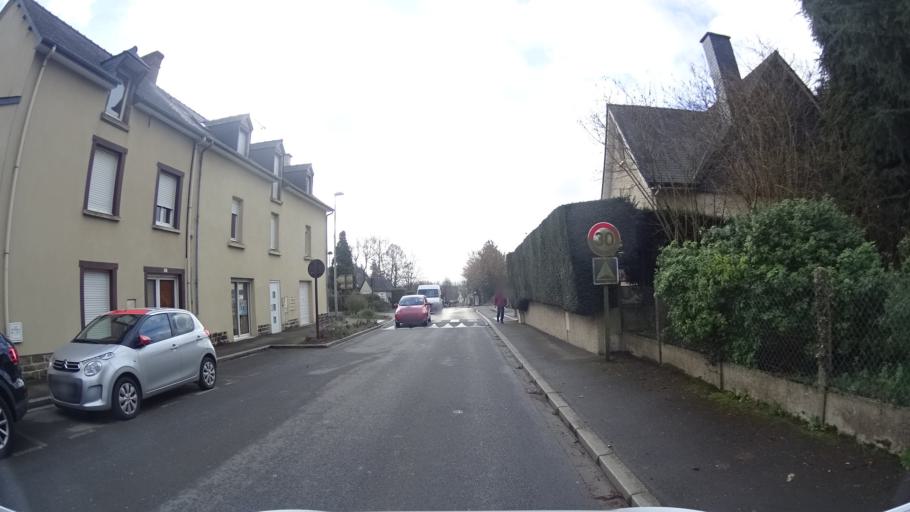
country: FR
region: Brittany
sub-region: Departement d'Ille-et-Vilaine
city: Romille
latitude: 48.2130
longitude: -1.8913
